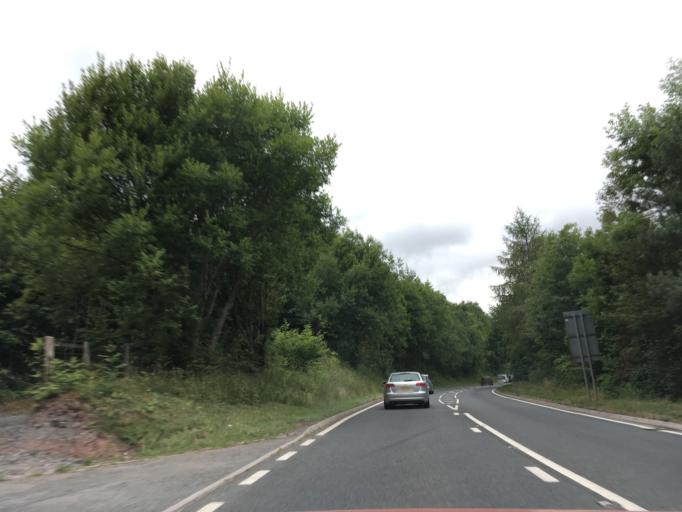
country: GB
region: Wales
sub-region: Sir Powys
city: Brecon
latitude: 51.9526
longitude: -3.4538
